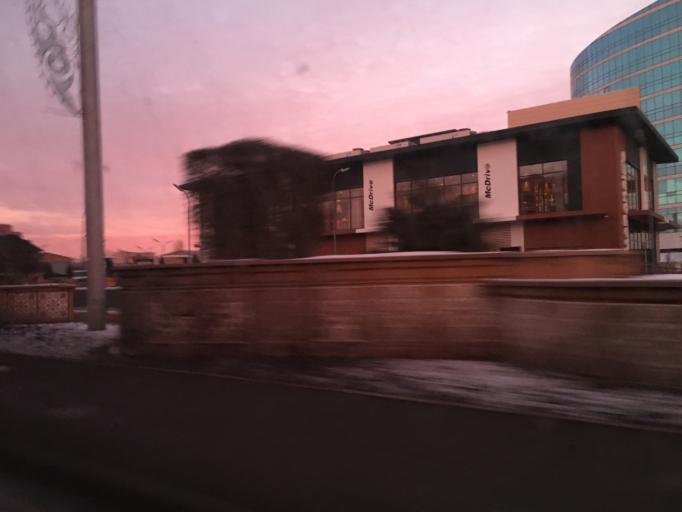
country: KZ
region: Astana Qalasy
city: Astana
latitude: 51.1372
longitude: 71.4164
